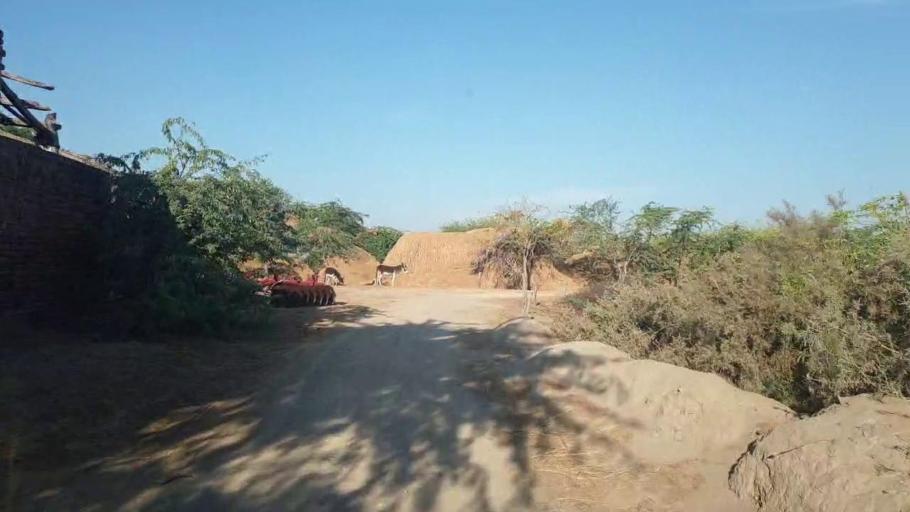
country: PK
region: Sindh
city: Talhar
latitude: 24.8190
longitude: 68.8386
